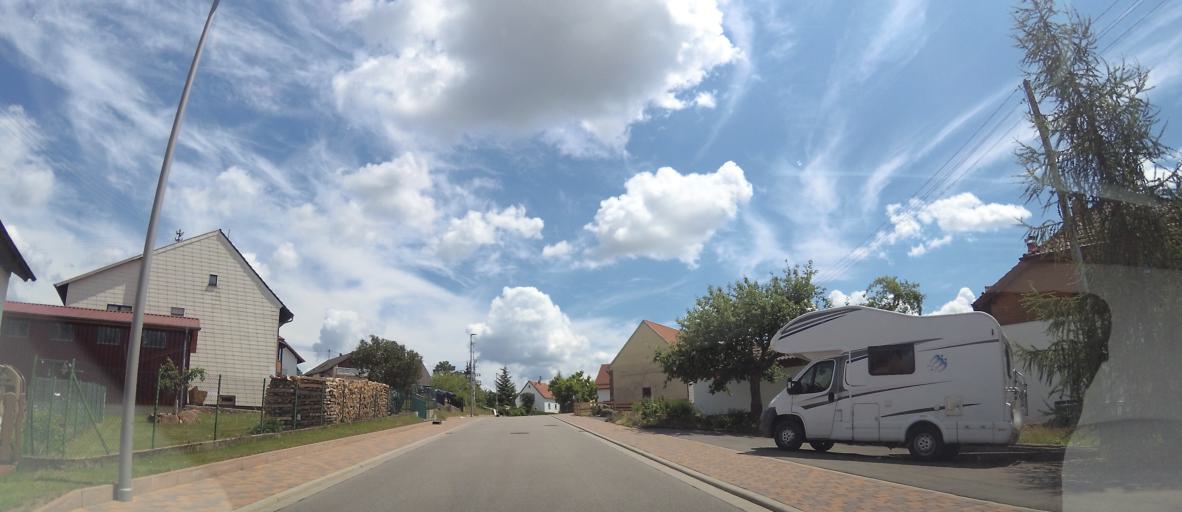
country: DE
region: Rheinland-Pfalz
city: Kleinsteinhausen
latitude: 49.2029
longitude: 7.4693
